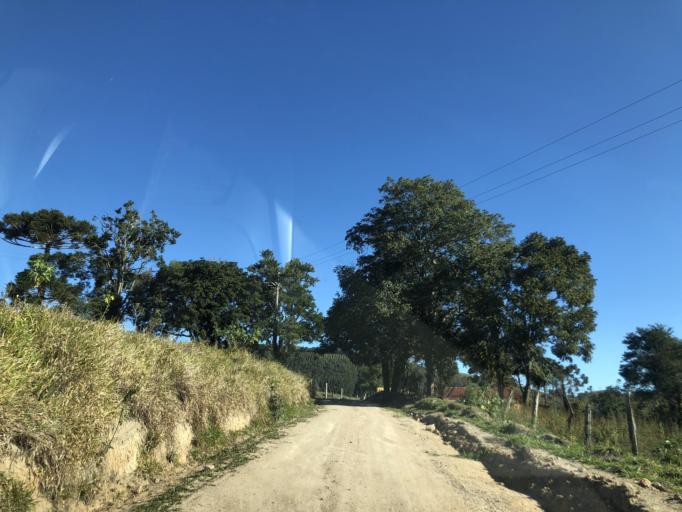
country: BR
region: Sao Paulo
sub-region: Pilar Do Sul
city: Pilar do Sul
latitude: -23.8288
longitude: -47.6254
